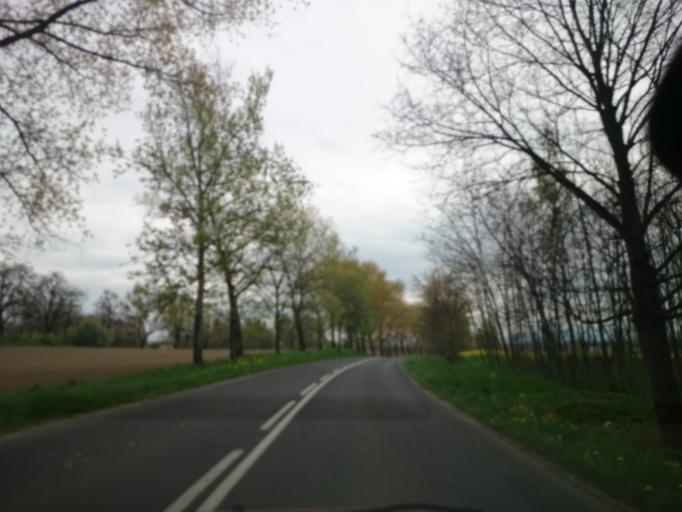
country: PL
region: Opole Voivodeship
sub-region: Powiat nyski
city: Nysa
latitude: 50.4265
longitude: 17.3408
